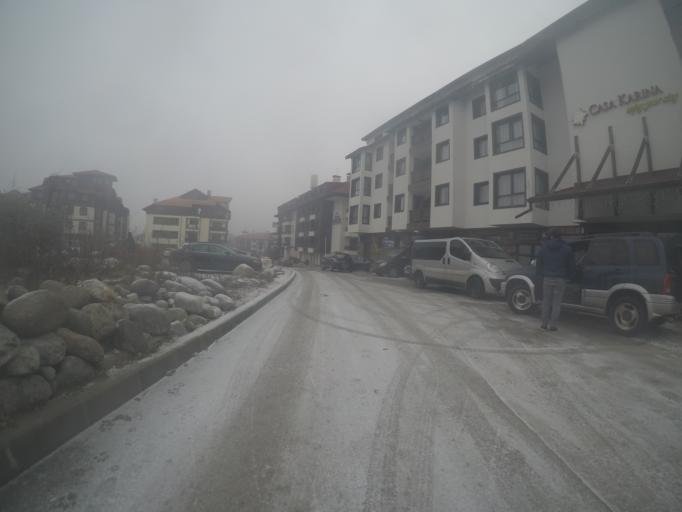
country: BG
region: Blagoevgrad
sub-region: Obshtina Bansko
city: Bansko
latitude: 41.8252
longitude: 23.4793
